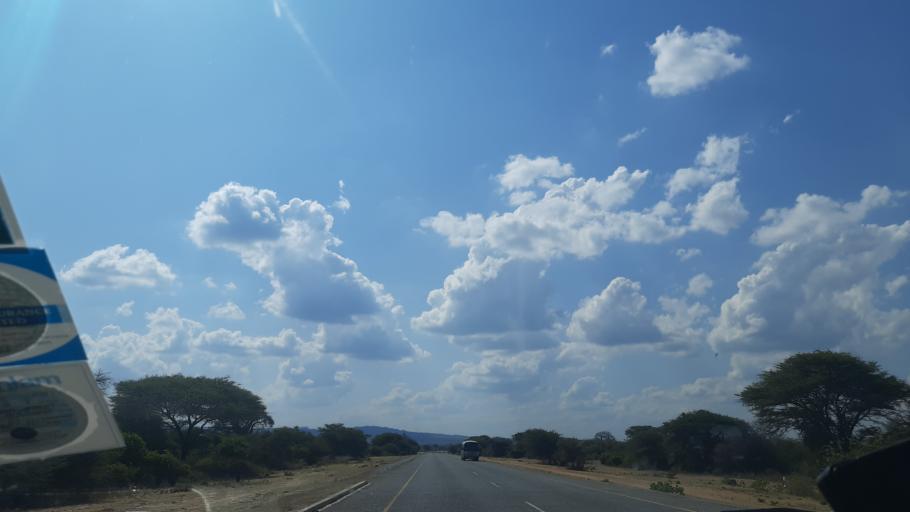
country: TZ
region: Singida
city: Kilimatinde
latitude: -5.8366
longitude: 35.0639
